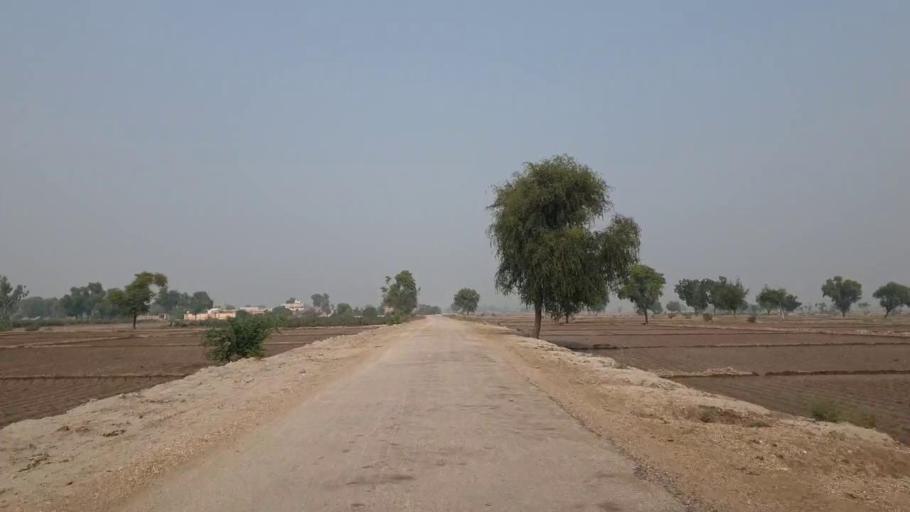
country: PK
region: Sindh
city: Bhan
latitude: 26.5111
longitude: 67.6895
